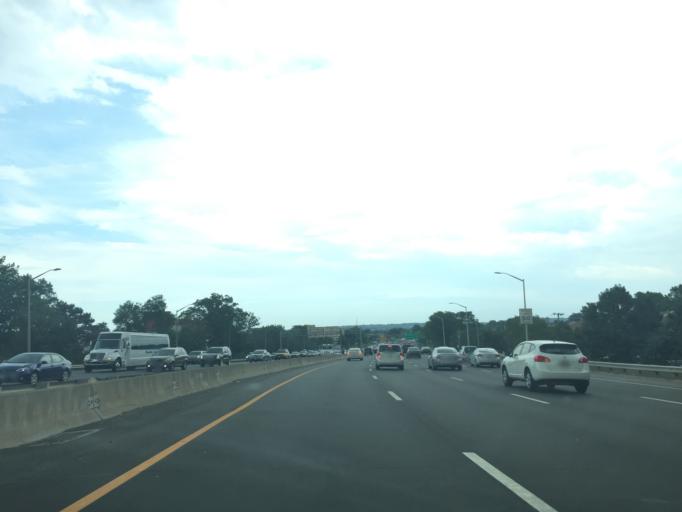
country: US
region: New York
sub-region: Richmond County
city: Bloomfield
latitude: 40.6208
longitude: -74.1682
